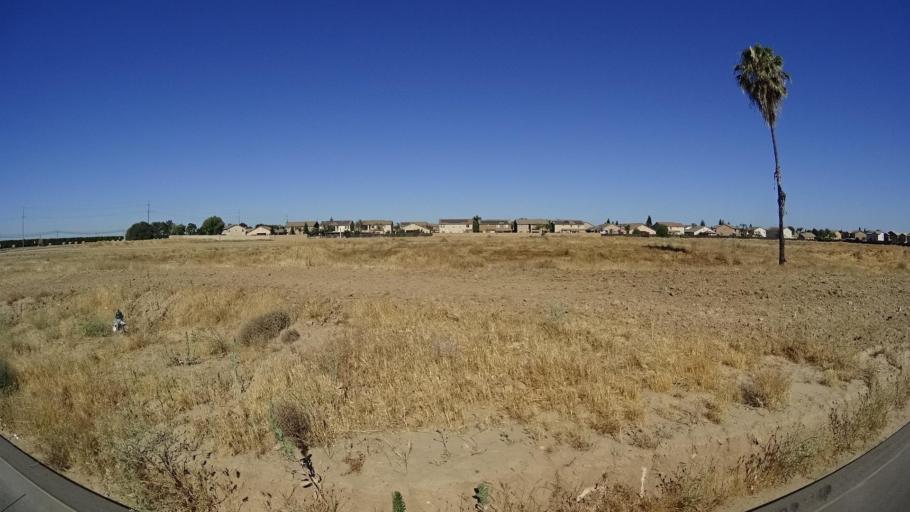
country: US
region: California
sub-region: Fresno County
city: Sunnyside
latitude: 36.7088
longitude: -119.6818
